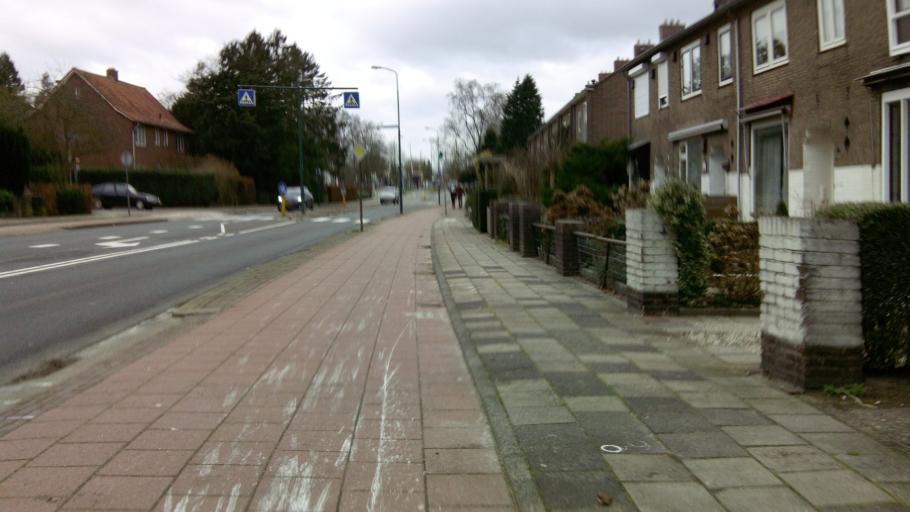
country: NL
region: Utrecht
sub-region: Gemeente Soest
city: Soest
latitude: 52.1639
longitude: 5.3050
